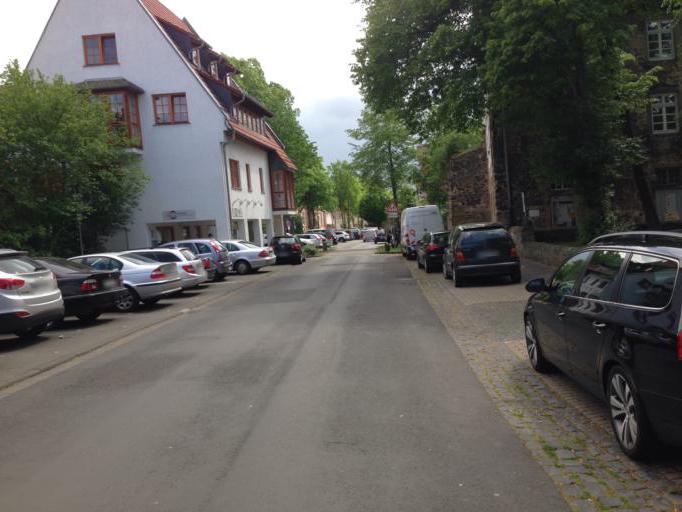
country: DE
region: Hesse
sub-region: Regierungsbezirk Giessen
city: Alsfeld
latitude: 50.7499
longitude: 9.2706
